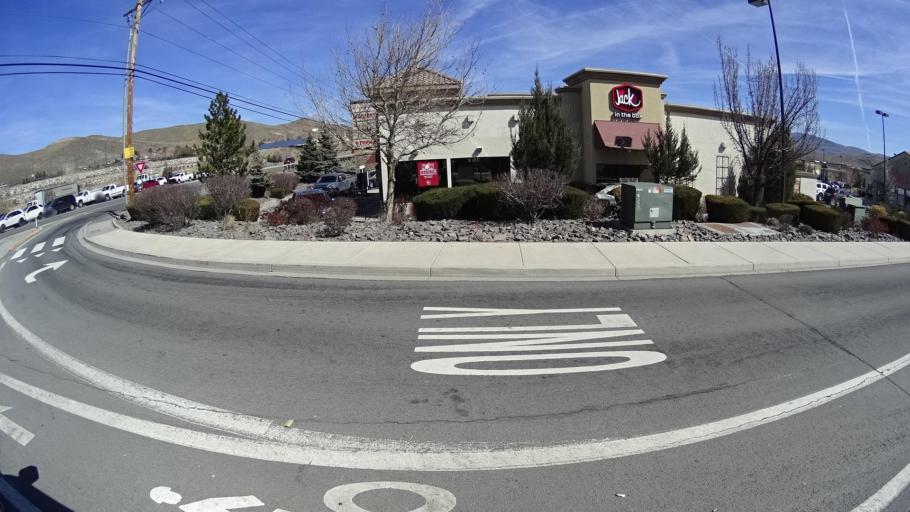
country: US
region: Nevada
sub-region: Washoe County
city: Sun Valley
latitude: 39.5834
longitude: -119.7427
